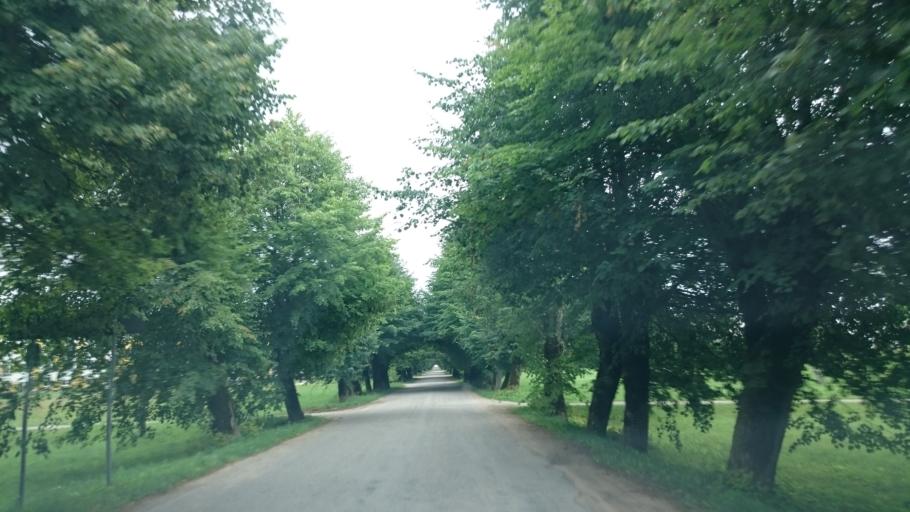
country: LV
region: Durbe
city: Liegi
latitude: 56.7341
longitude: 21.3870
